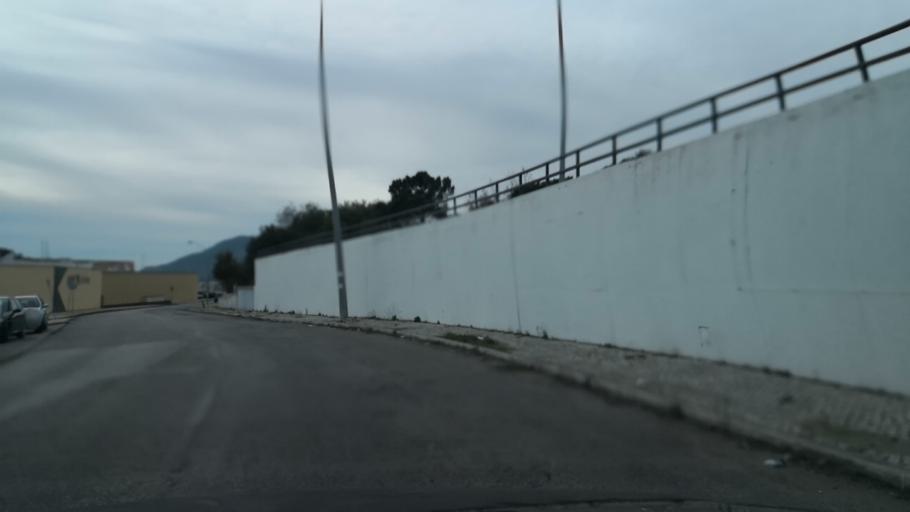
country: PT
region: Setubal
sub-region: Setubal
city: Setubal
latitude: 38.5387
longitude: -8.8750
